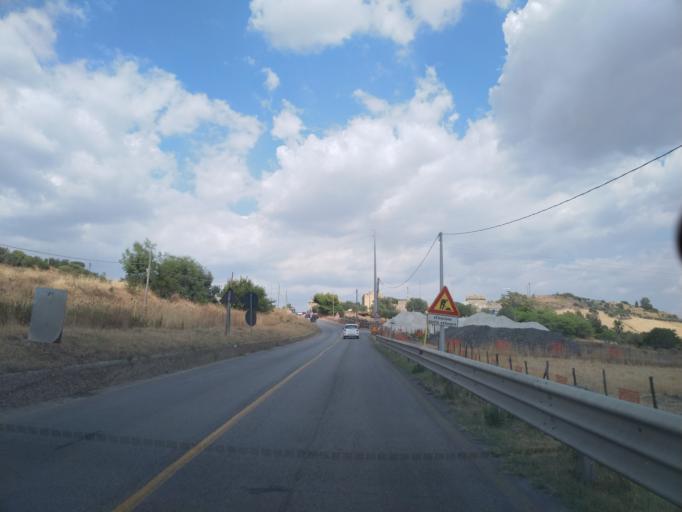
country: IT
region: Sicily
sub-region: Provincia di Caltanissetta
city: San Cataldo
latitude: 37.4554
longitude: 13.9906
